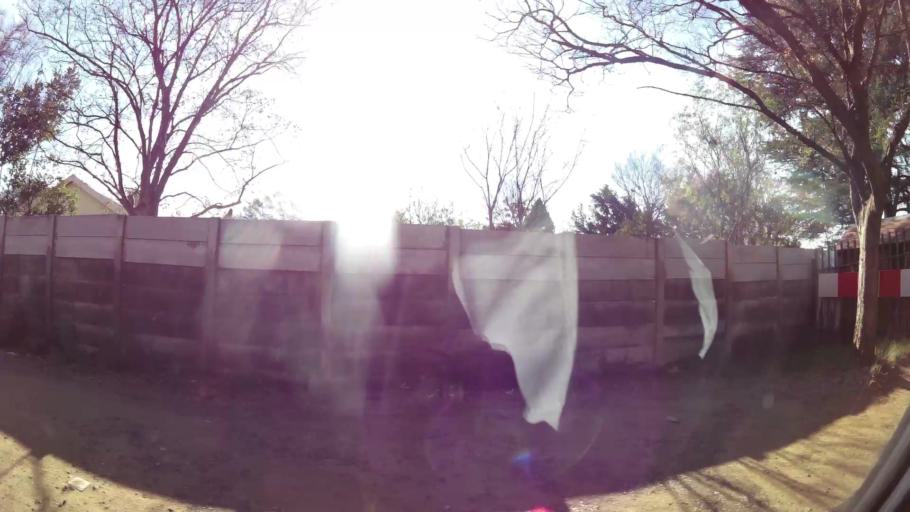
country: ZA
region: Gauteng
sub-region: City of Johannesburg Metropolitan Municipality
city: Roodepoort
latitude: -26.0969
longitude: 27.9777
